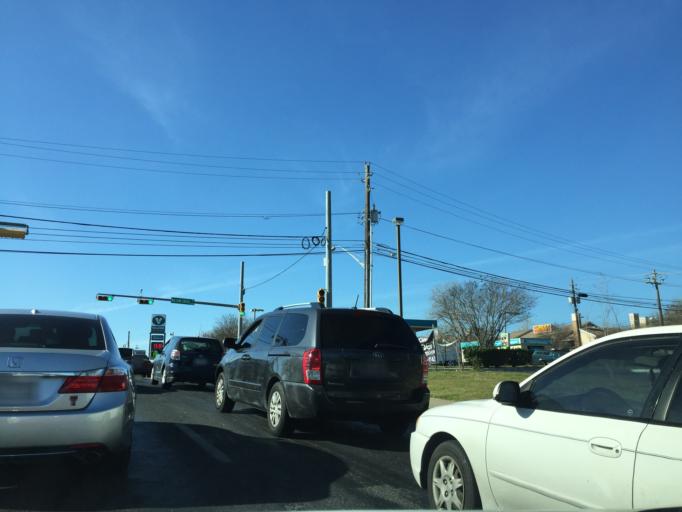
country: US
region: Texas
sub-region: Travis County
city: Austin
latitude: 30.2296
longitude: -97.7306
